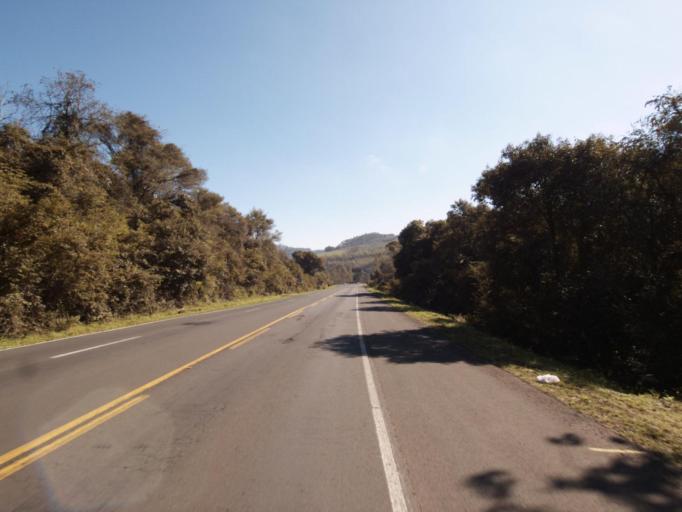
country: BR
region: Rio Grande do Sul
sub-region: Frederico Westphalen
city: Frederico Westphalen
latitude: -27.0828
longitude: -53.2230
